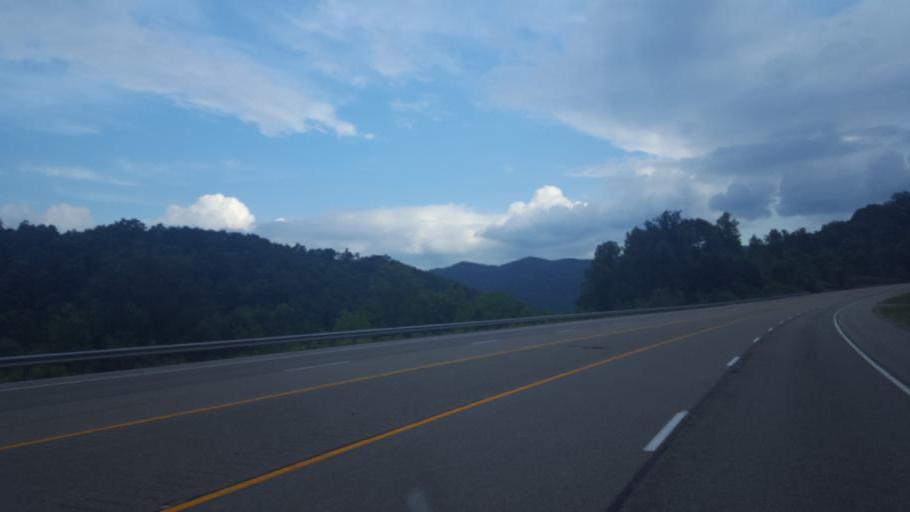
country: US
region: Kentucky
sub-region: Letcher County
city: Jenkins
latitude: 37.2015
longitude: -82.6223
